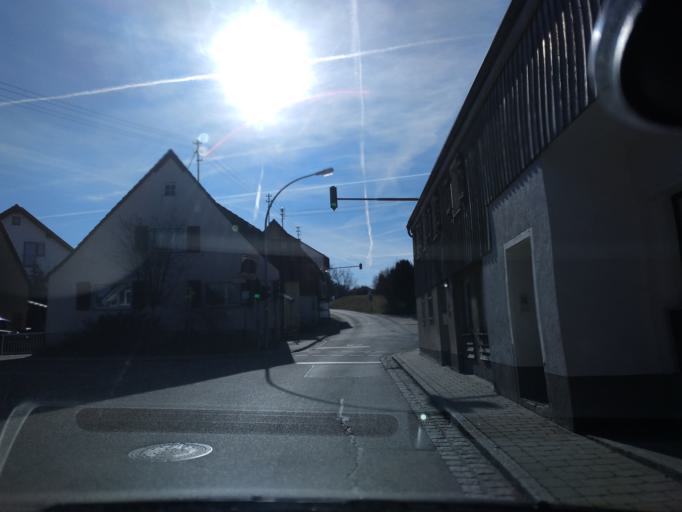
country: DE
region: Baden-Wuerttemberg
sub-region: Regierungsbezirk Stuttgart
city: Mainhardt
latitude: 49.0801
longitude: 9.5574
